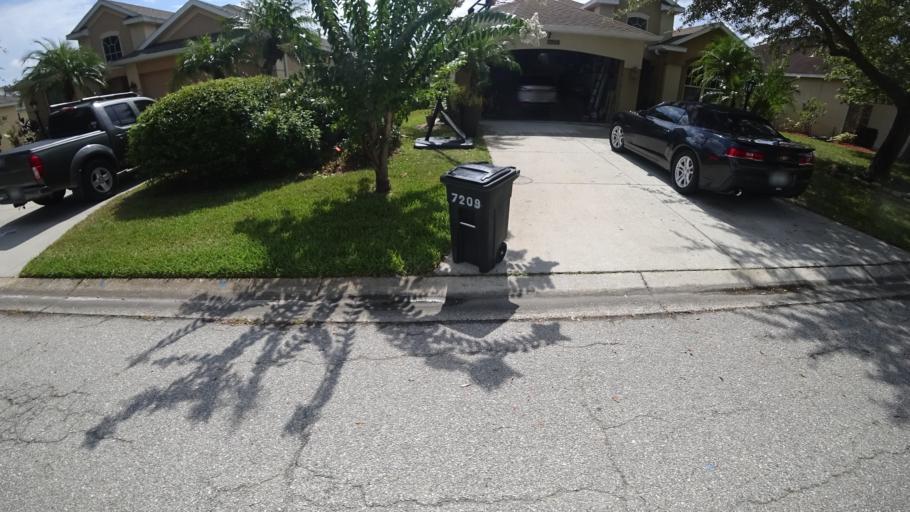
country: US
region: Florida
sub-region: Sarasota County
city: The Meadows
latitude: 27.4118
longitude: -82.4262
